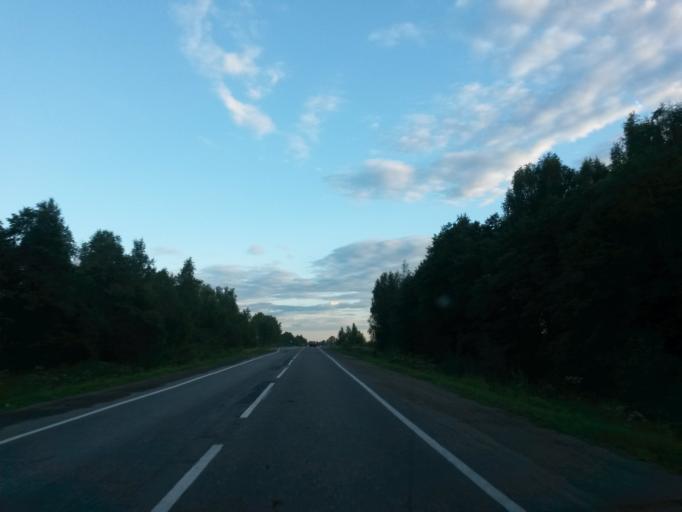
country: RU
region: Jaroslavl
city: Gavrilov-Yam
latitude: 57.3639
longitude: 39.9080
